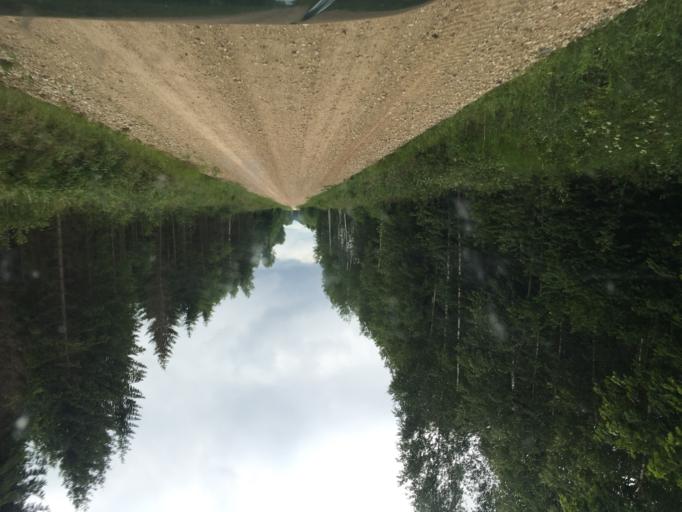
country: LV
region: Vilaka
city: Vilaka
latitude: 57.3819
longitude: 27.5226
